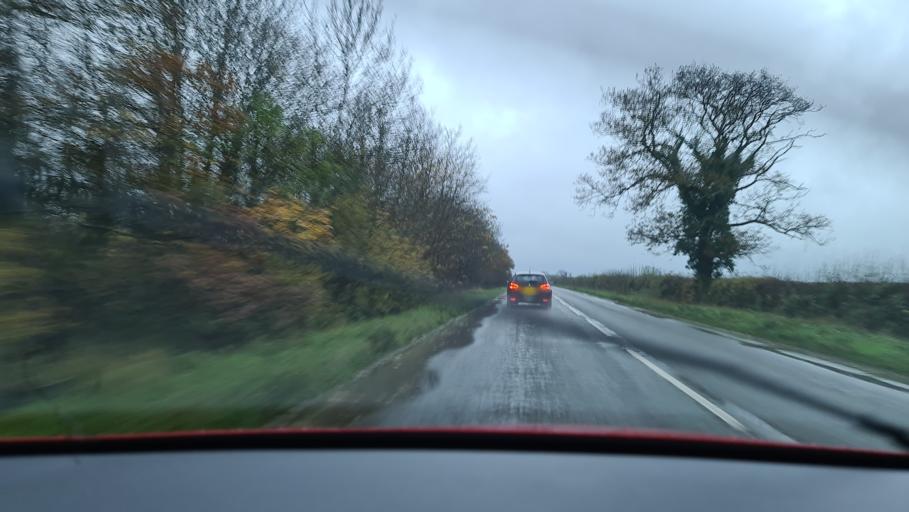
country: GB
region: England
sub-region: Oxfordshire
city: Somerton
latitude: 51.9290
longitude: -1.2181
